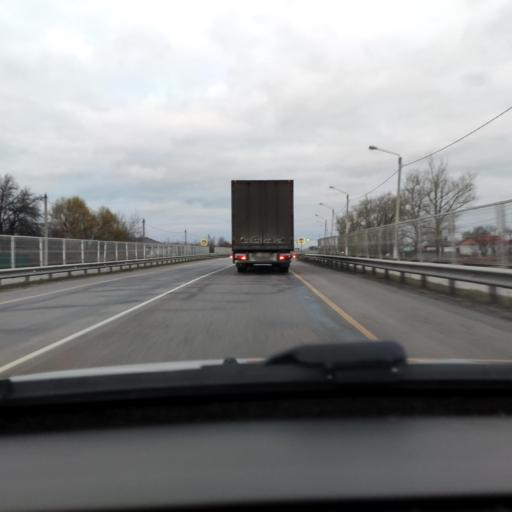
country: RU
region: Lipetsk
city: Khlevnoye
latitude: 52.2629
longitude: 39.1577
